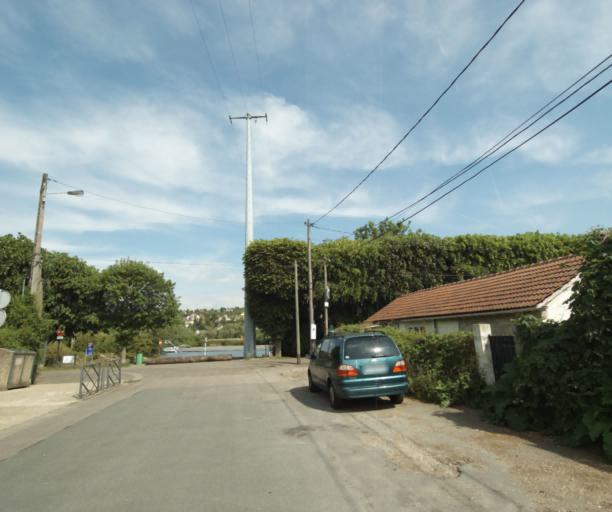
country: FR
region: Ile-de-France
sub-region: Departement des Yvelines
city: Mezy-sur-Seine
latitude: 48.9955
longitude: 1.8943
